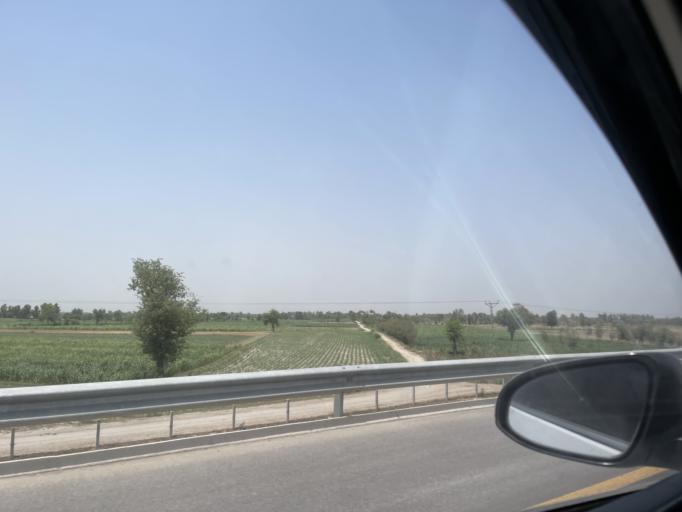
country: PK
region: Sindh
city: Ghotki
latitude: 28.0207
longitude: 69.2932
